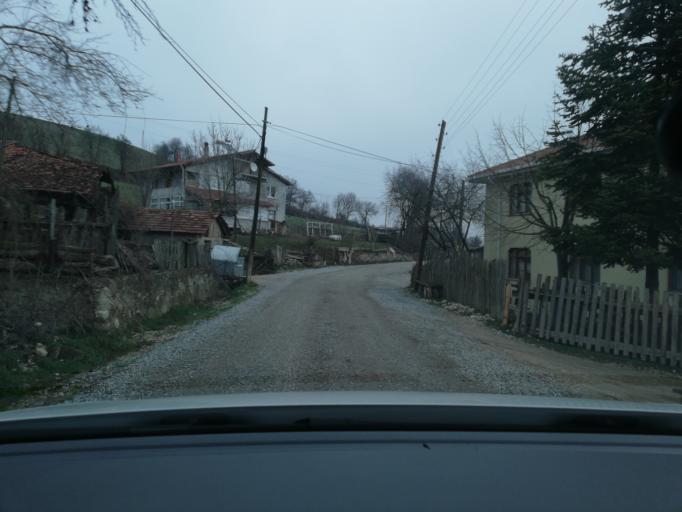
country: TR
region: Bolu
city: Bolu
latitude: 40.6644
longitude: 31.4618
